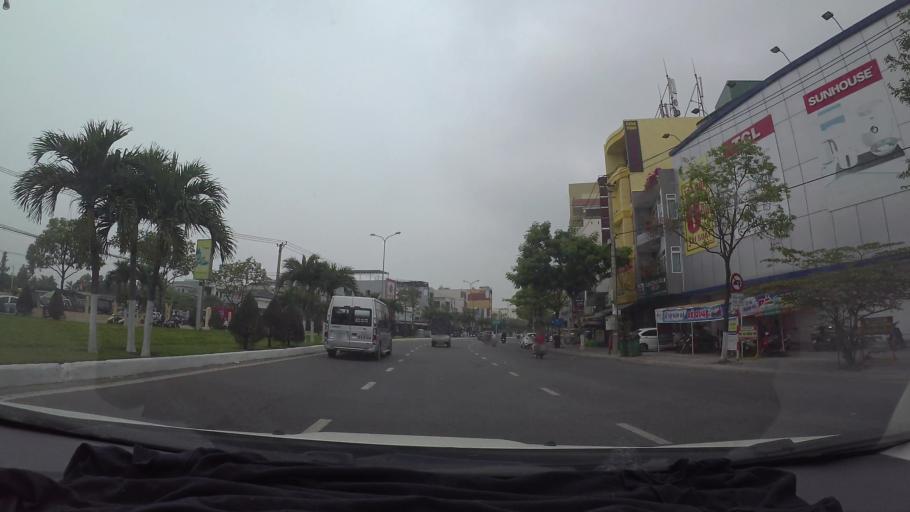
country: VN
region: Da Nang
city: Cam Le
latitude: 16.0317
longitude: 108.2089
